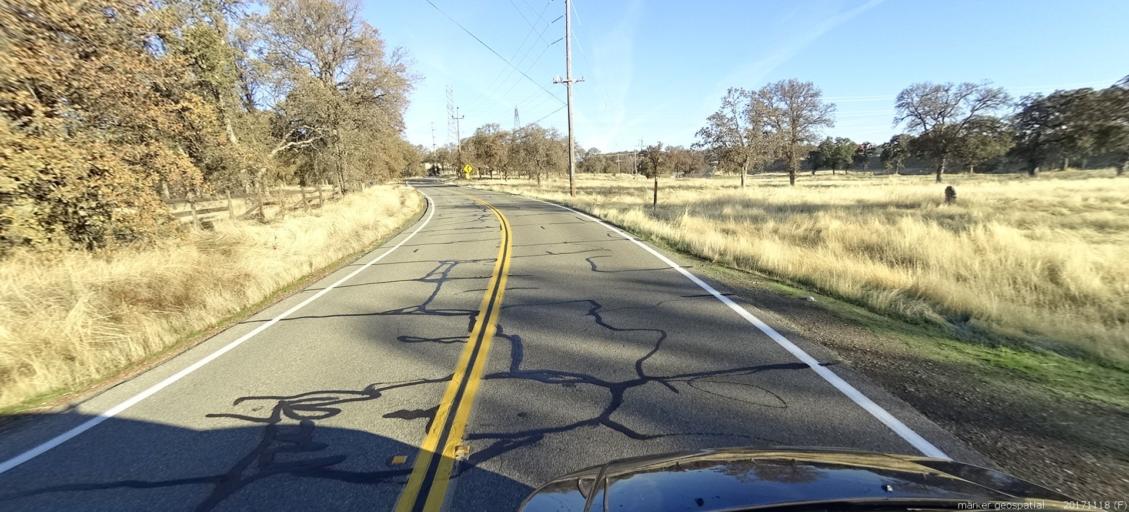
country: US
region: California
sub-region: Shasta County
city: Cottonwood
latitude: 40.4036
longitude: -122.2829
